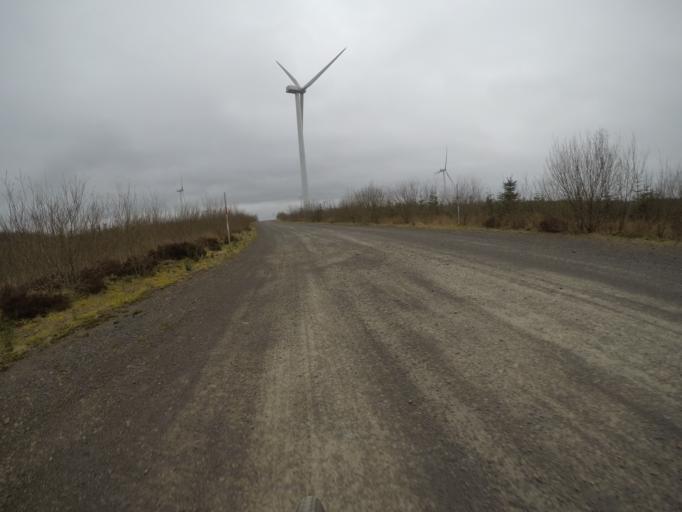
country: GB
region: Scotland
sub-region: East Ayrshire
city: Newmilns
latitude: 55.6565
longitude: -4.3246
